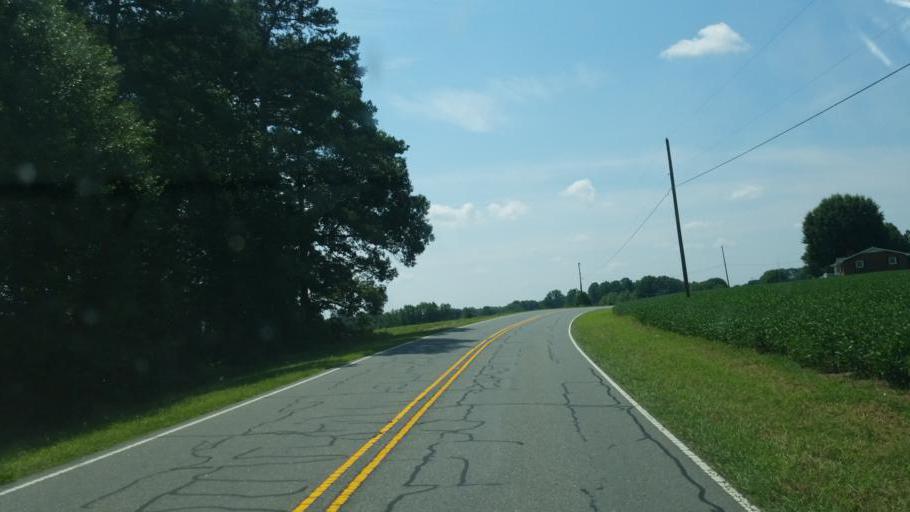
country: US
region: North Carolina
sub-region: Gaston County
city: Cherryville
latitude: 35.4823
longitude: -81.4445
